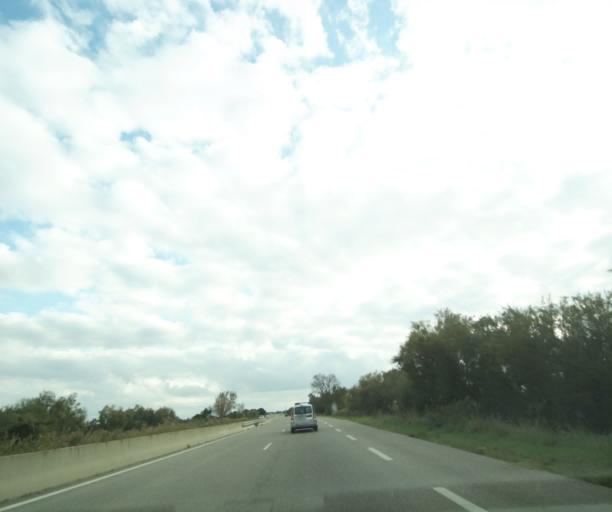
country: FR
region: Languedoc-Roussillon
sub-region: Departement du Gard
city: Aigues-Mortes
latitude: 43.6014
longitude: 4.1944
